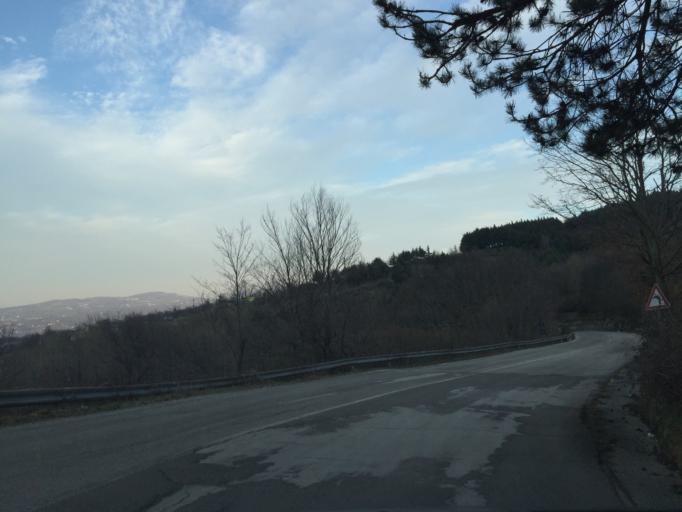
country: IT
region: Molise
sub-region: Provincia di Campobasso
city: Guardiaregia
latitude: 41.4341
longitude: 14.5448
